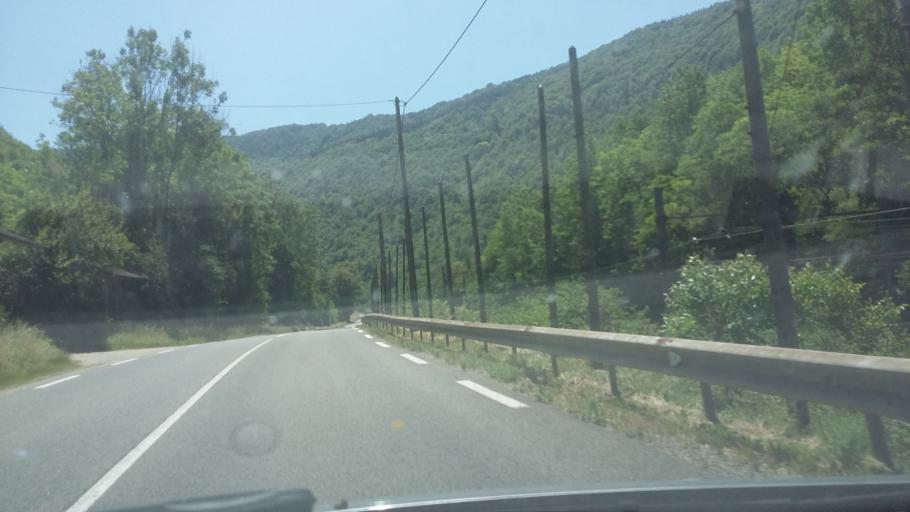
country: FR
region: Rhone-Alpes
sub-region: Departement de l'Ain
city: Tenay
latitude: 45.9075
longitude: 5.5124
